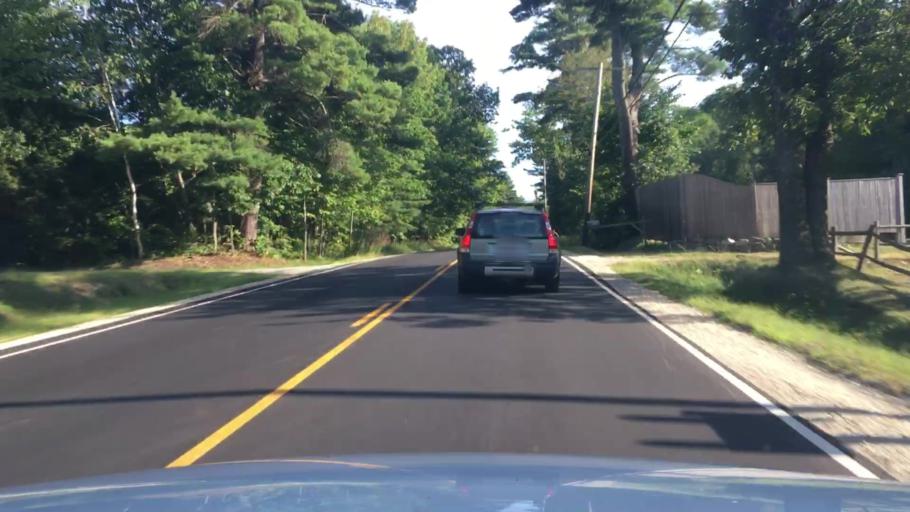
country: US
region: Maine
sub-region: Cumberland County
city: Cumberland Center
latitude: 43.7742
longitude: -70.3018
